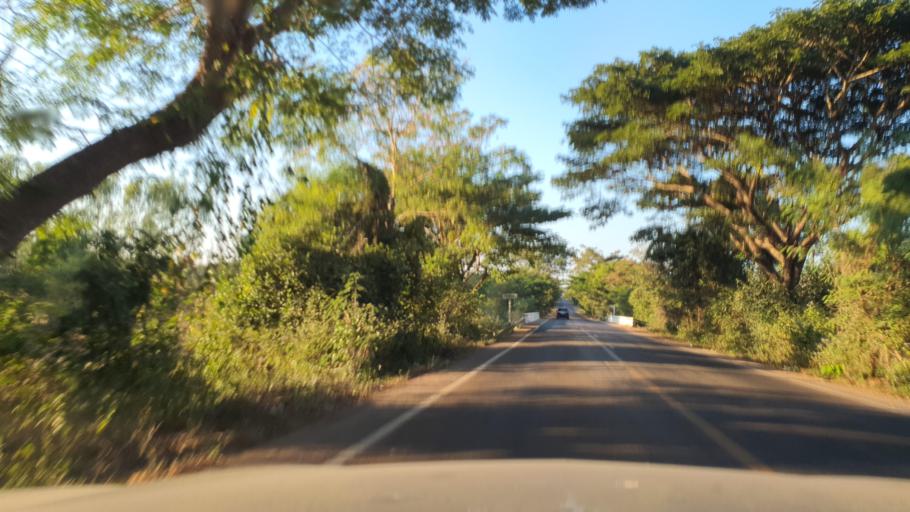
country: TH
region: Nakhon Phanom
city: Si Songkhram
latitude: 17.5658
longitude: 104.2351
